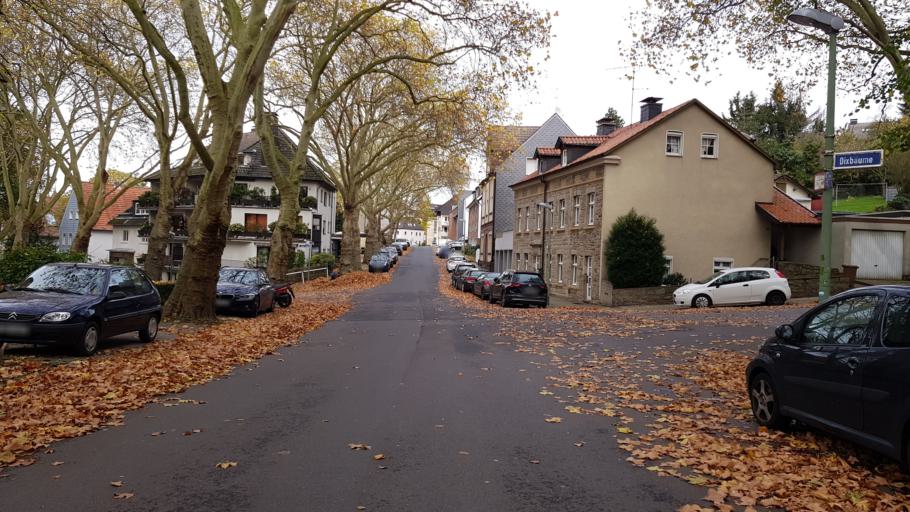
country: DE
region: North Rhine-Westphalia
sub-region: Regierungsbezirk Dusseldorf
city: Velbert
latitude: 51.3898
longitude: 7.0872
